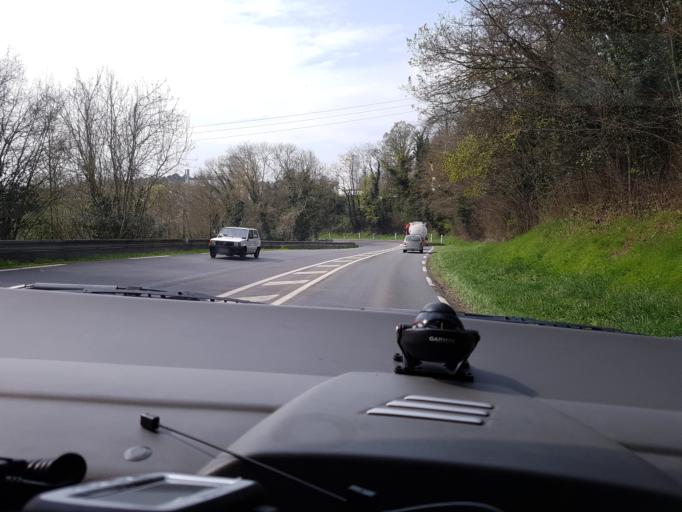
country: FR
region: Picardie
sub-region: Departement de l'Aisne
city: Cuffies
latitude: 49.4075
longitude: 3.3371
